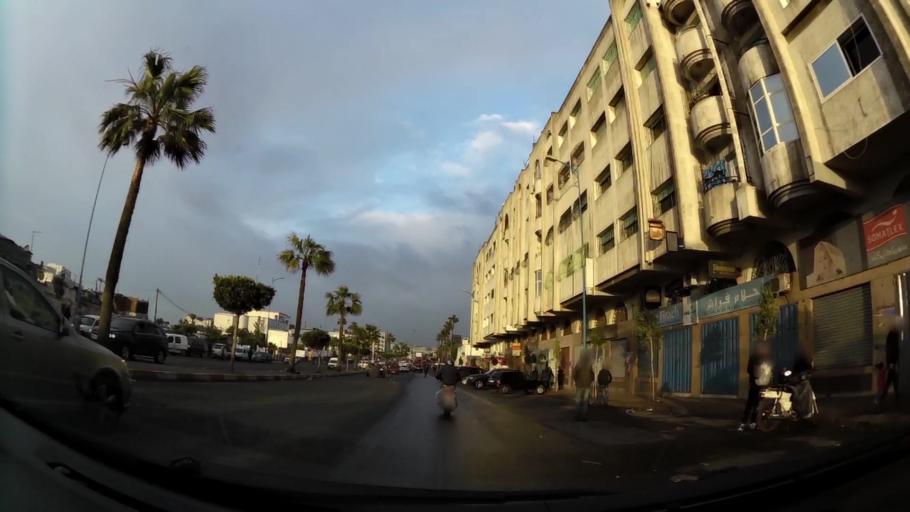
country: MA
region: Grand Casablanca
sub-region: Casablanca
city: Casablanca
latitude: 33.5619
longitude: -7.5979
